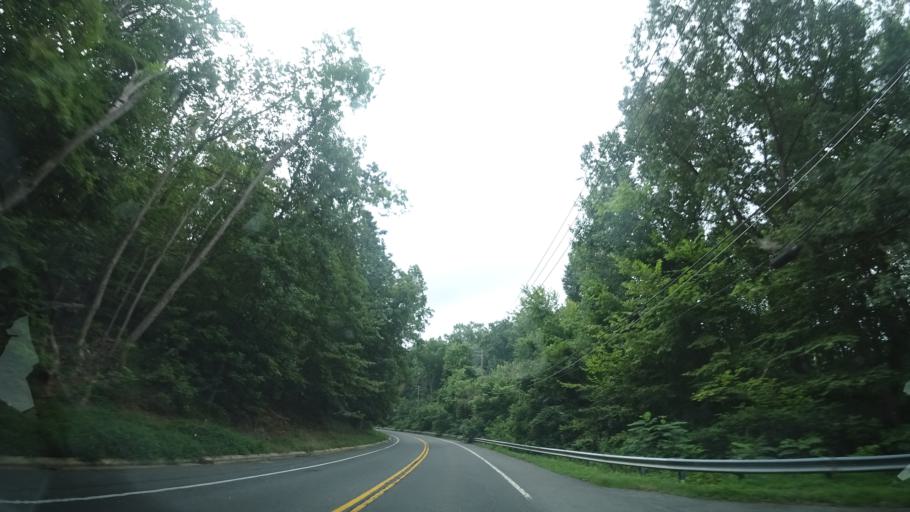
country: US
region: Virginia
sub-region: Loudoun County
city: Lowes Island
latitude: 39.0756
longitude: -77.3263
